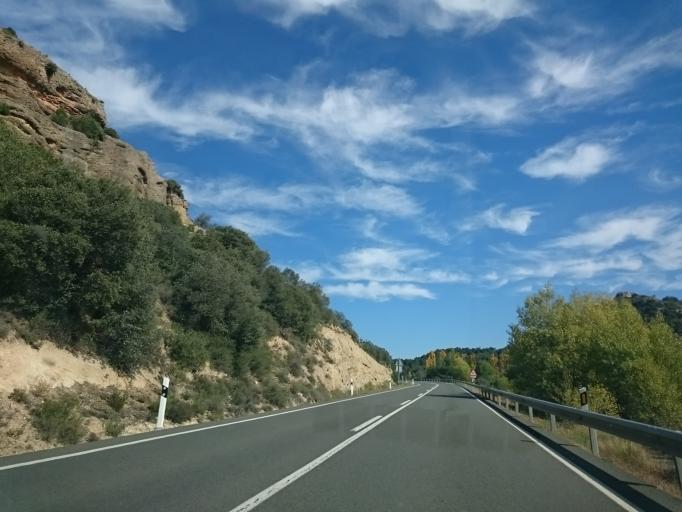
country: ES
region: Aragon
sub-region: Provincia de Huesca
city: Castigaleu
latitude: 42.1261
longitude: 0.6023
